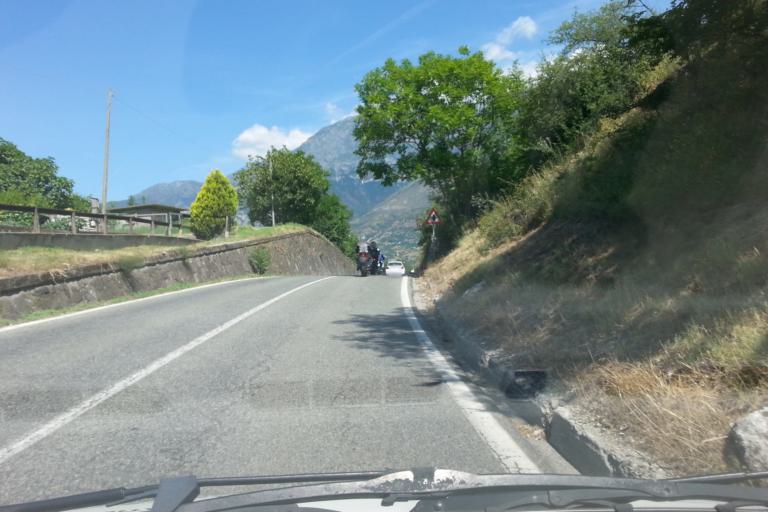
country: IT
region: Piedmont
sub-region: Provincia di Torino
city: San Giorio
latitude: 45.1249
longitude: 7.1844
